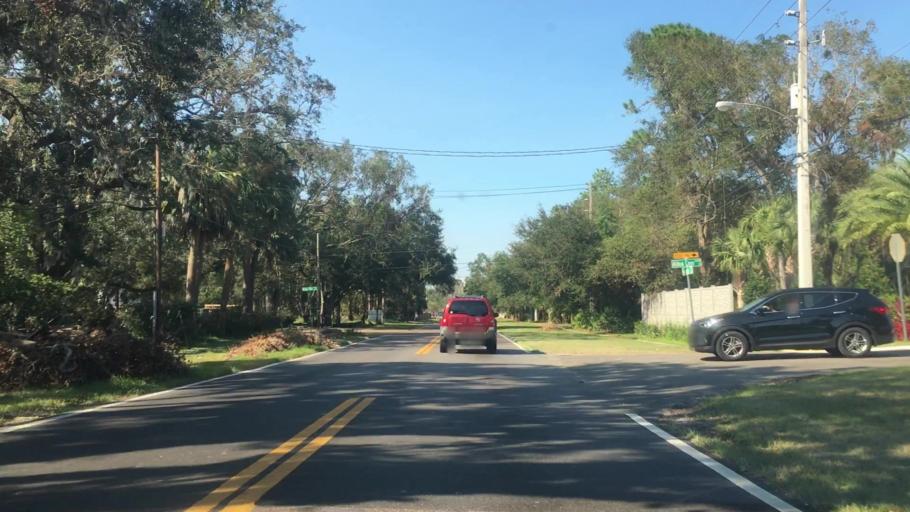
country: US
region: Florida
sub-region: Duval County
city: Jacksonville Beach
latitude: 30.2950
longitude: -81.4378
